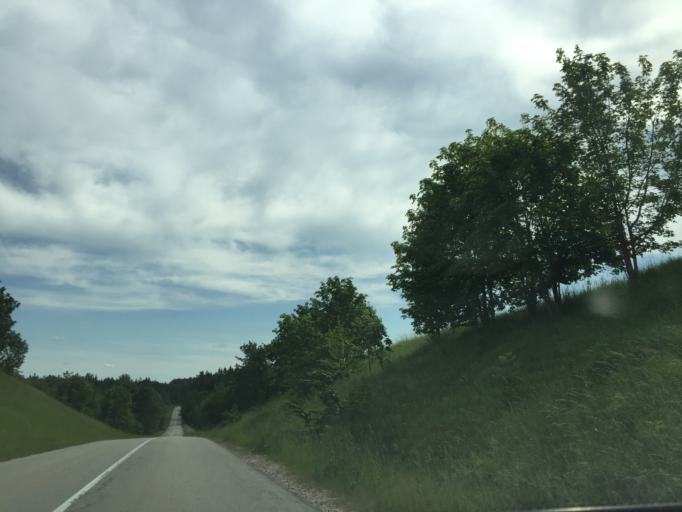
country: LV
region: Tukuma Rajons
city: Tukums
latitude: 57.0295
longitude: 23.2507
